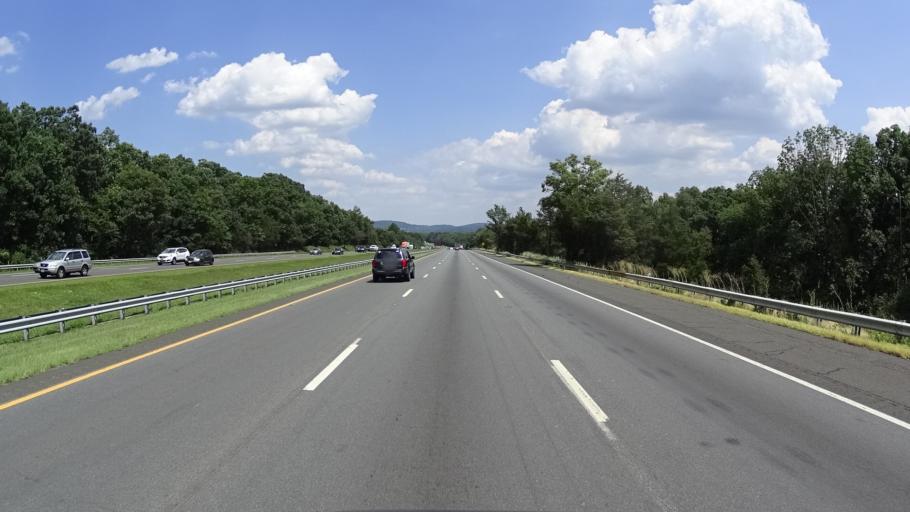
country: US
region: New Jersey
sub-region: Somerset County
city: Bedminster
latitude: 40.6431
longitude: -74.6930
